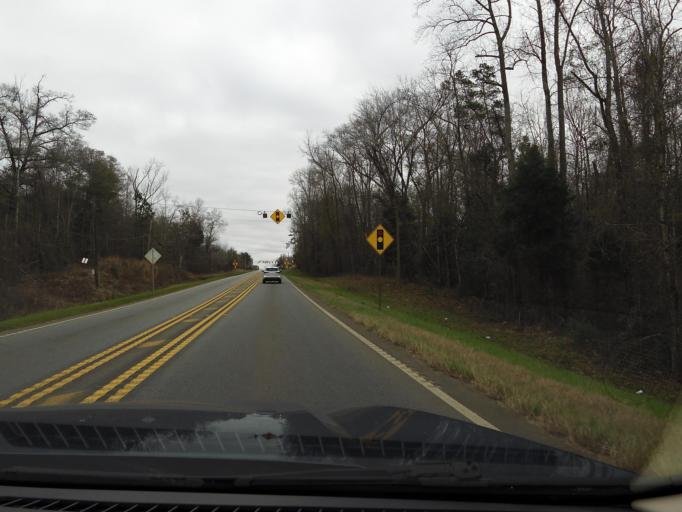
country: US
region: Georgia
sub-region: Randolph County
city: Cuthbert
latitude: 31.7700
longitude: -84.7757
